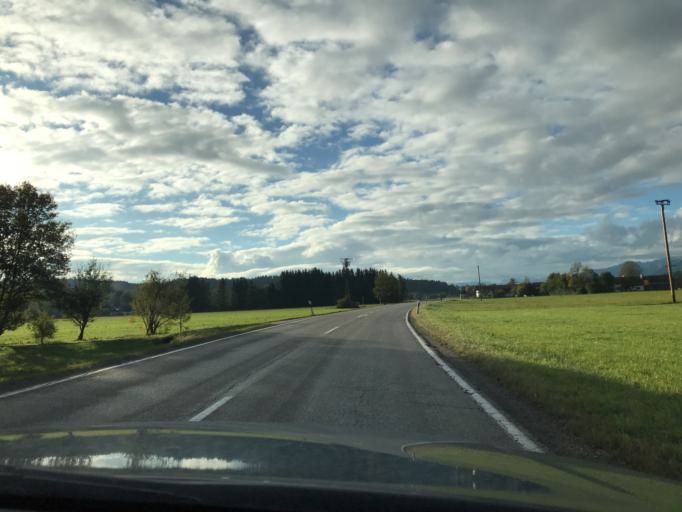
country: DE
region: Bavaria
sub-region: Upper Bavaria
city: Geretsried
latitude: 47.8388
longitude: 11.5290
